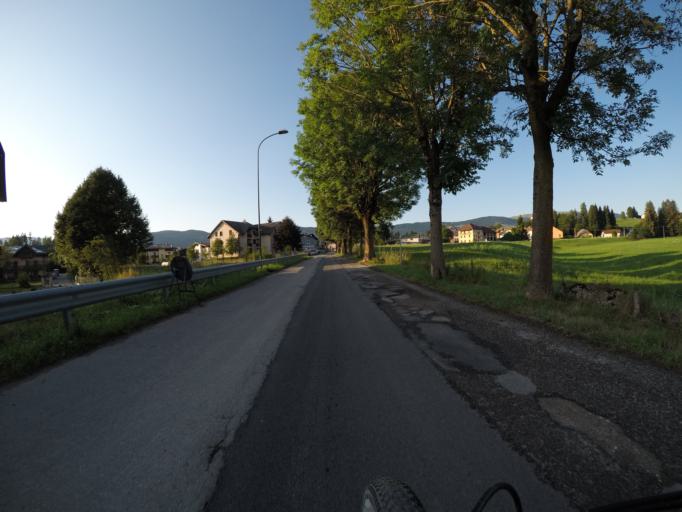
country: IT
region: Veneto
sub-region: Provincia di Vicenza
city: Asiago
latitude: 45.8681
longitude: 11.5107
